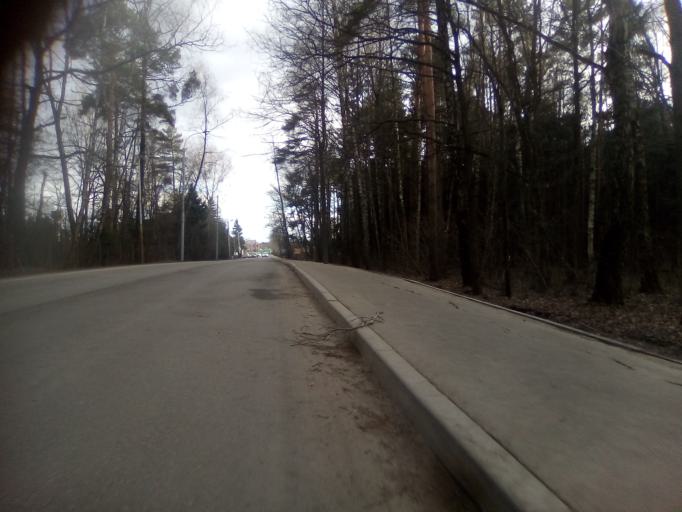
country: RU
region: Moskovskaya
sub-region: Leninskiy Rayon
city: Vnukovo
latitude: 55.5976
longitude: 37.3198
